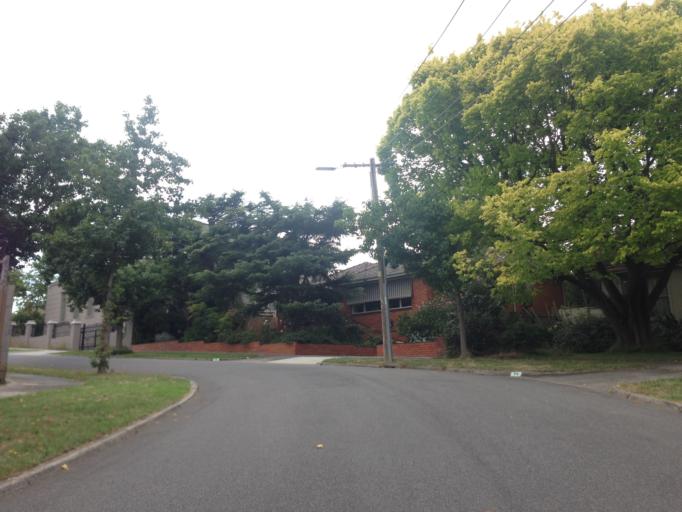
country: AU
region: Victoria
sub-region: Boroondara
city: Balwyn North
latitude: -37.7981
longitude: 145.0908
